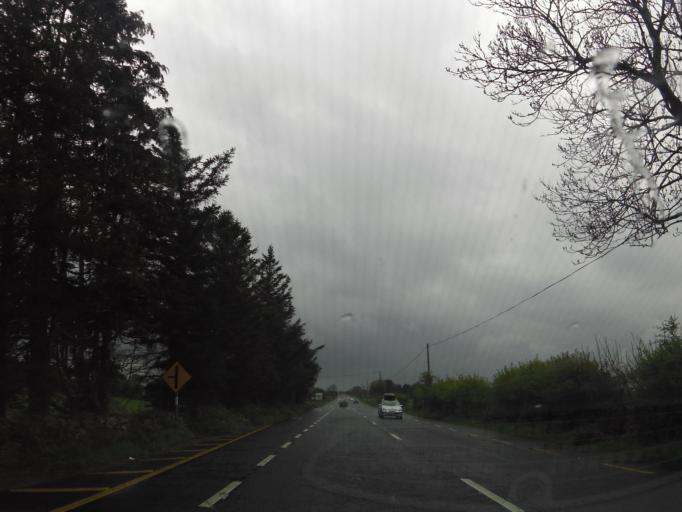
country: IE
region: Connaught
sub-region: County Galway
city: Claregalway
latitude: 53.3734
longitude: -8.9216
